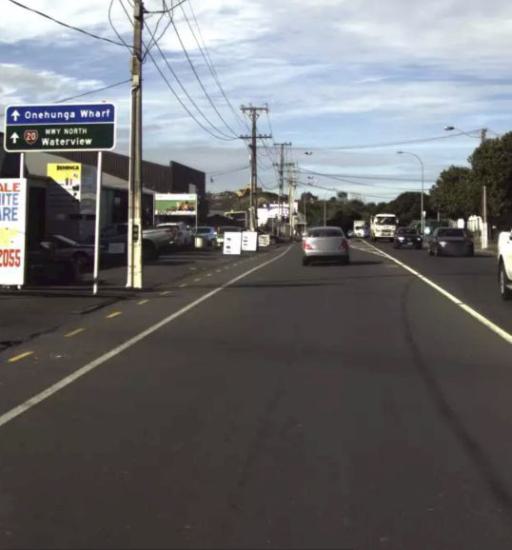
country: NZ
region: Auckland
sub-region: Auckland
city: Mangere
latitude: -36.9284
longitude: 174.7864
